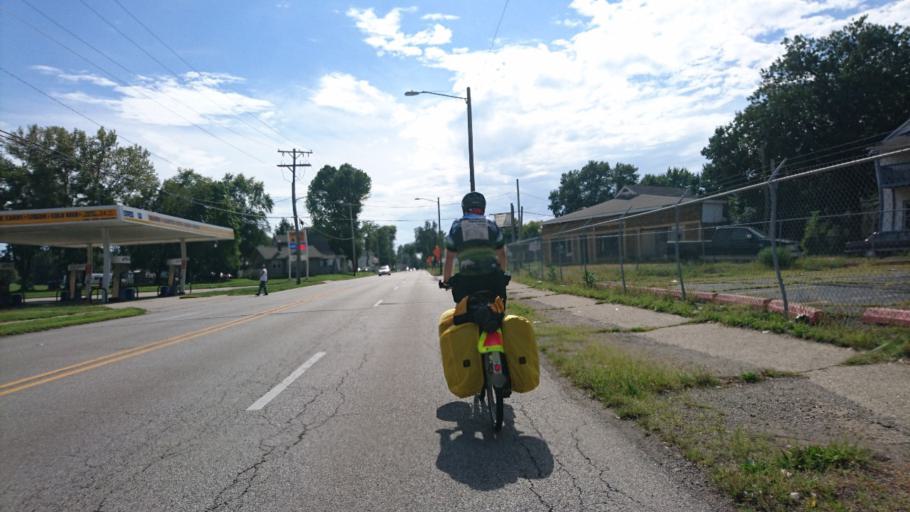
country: US
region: Illinois
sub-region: Sangamon County
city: Grandview
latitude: 39.8262
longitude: -89.6406
